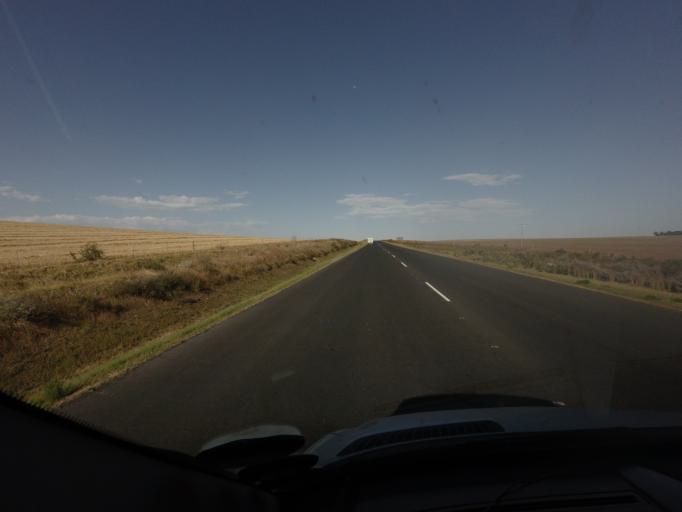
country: ZA
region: Western Cape
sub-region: Cape Winelands District Municipality
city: Ashton
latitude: -34.1411
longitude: 20.0119
